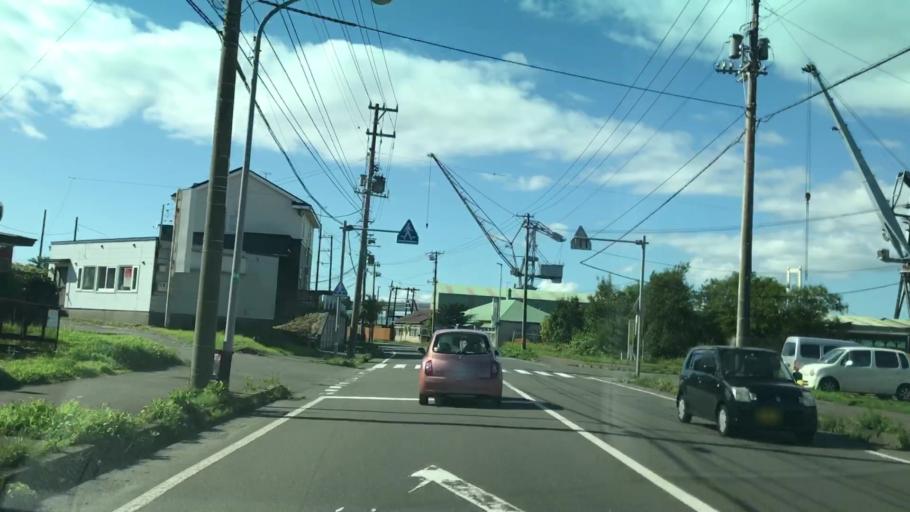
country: JP
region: Hokkaido
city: Muroran
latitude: 42.3376
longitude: 140.9558
